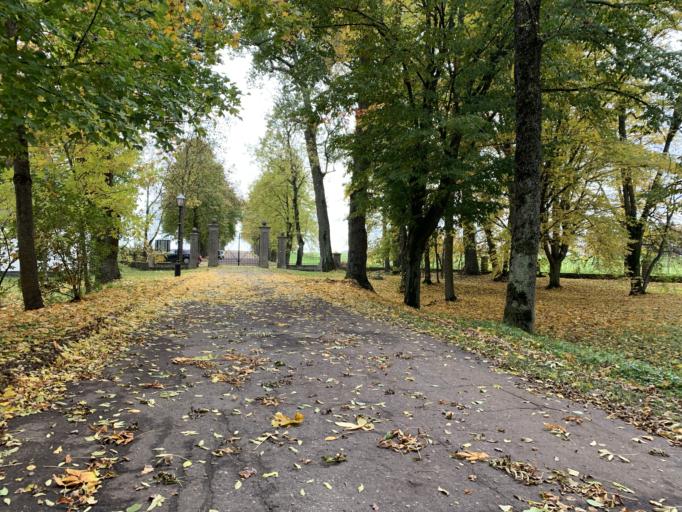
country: BY
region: Minsk
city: Nyasvizh
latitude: 53.2216
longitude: 26.7012
